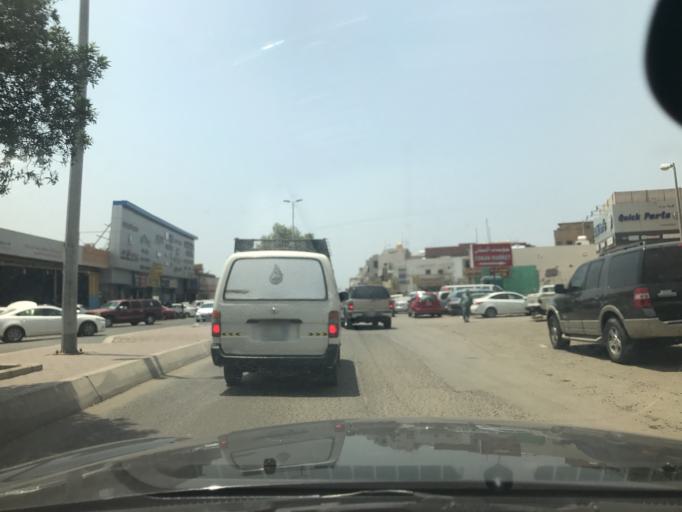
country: SA
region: Makkah
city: Jeddah
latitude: 21.4594
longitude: 39.2264
